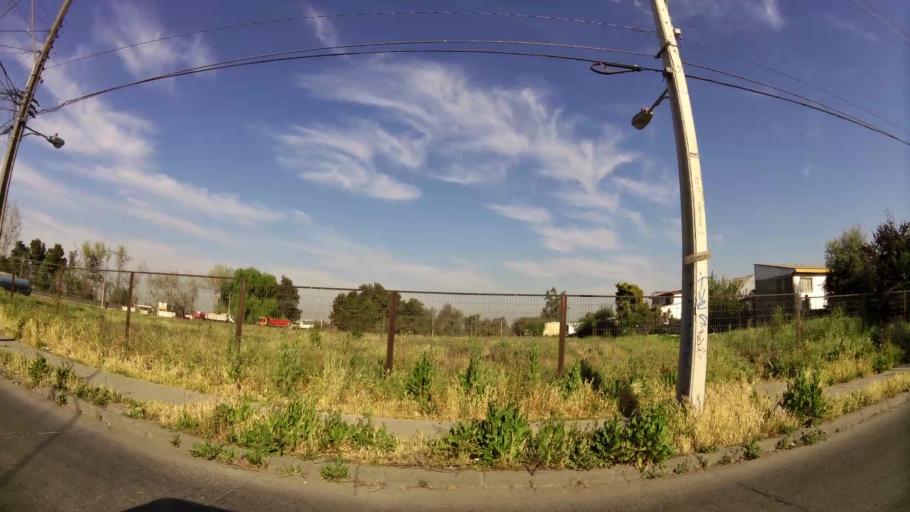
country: CL
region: Santiago Metropolitan
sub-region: Provincia de Santiago
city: La Pintana
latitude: -33.5690
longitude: -70.5924
